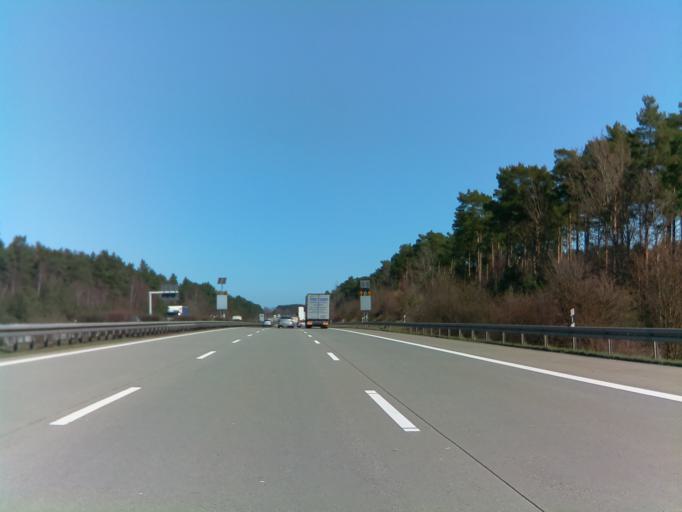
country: DE
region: Brandenburg
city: Niemegk
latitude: 52.1010
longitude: 12.6998
